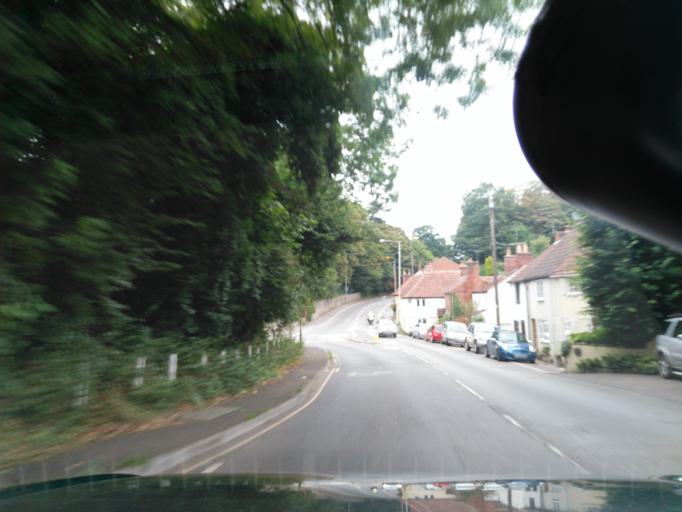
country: GB
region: England
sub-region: Wiltshire
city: Westbury
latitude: 51.2501
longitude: -2.1894
